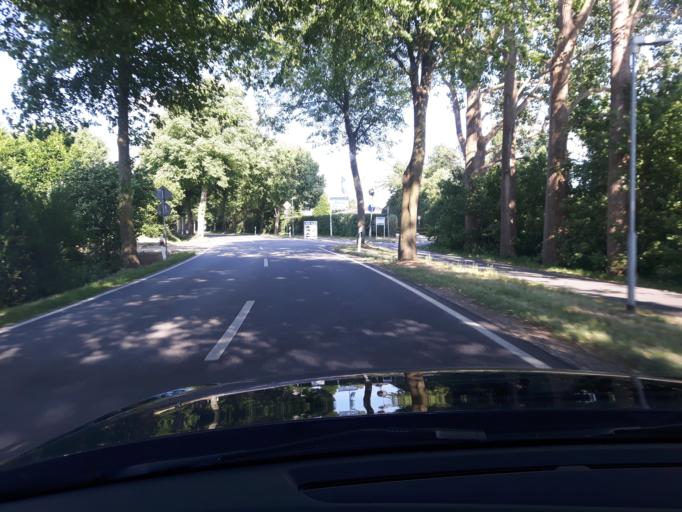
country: DE
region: Schleswig-Holstein
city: Neustadt in Holstein
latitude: 54.0913
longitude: 10.8394
